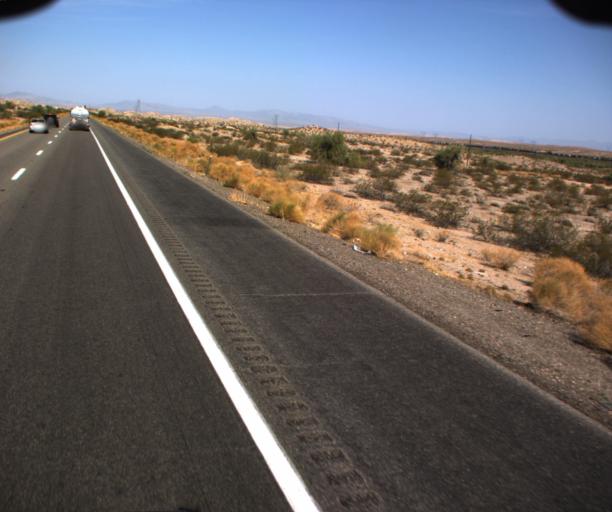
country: US
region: Arizona
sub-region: Mohave County
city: Desert Hills
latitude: 34.7279
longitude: -114.3740
